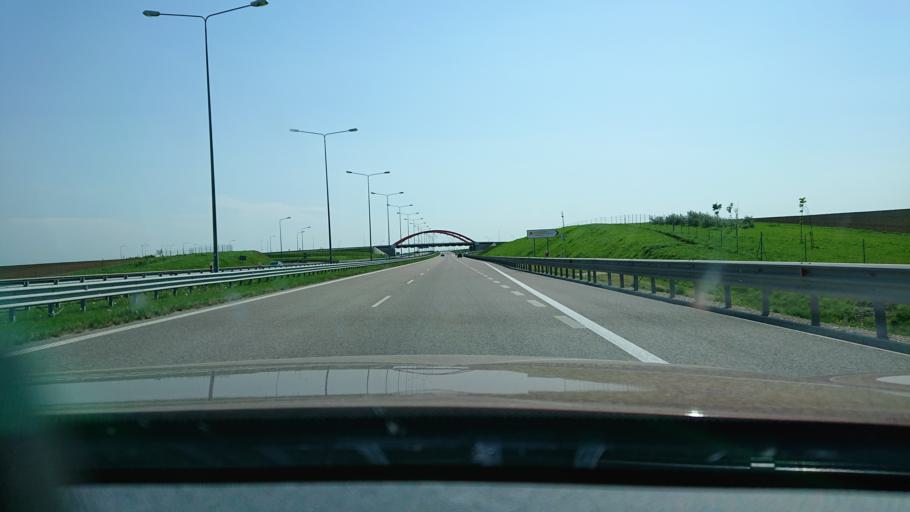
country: PL
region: Subcarpathian Voivodeship
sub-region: Powiat jaroslawski
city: Radymno
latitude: 49.9125
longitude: 22.8033
